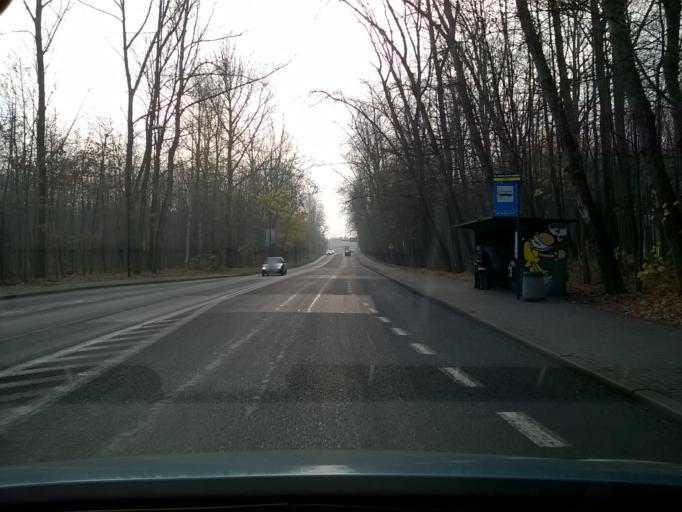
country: PL
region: Silesian Voivodeship
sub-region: Swietochlowice
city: Swietochlowice
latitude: 50.2584
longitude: 18.9361
